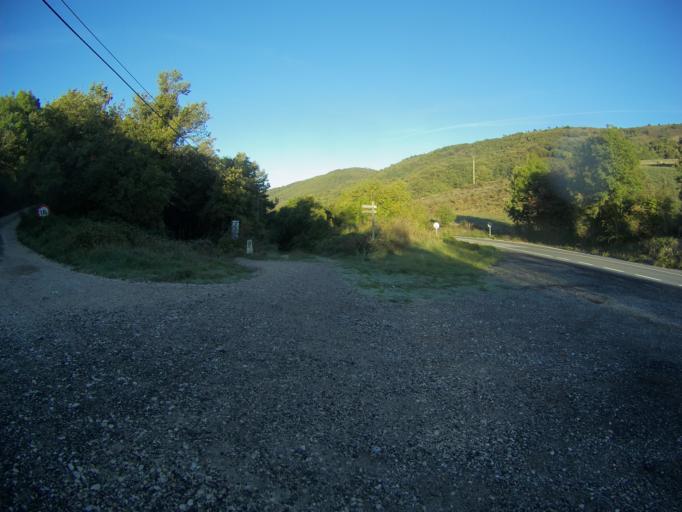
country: ES
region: Navarre
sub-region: Provincia de Navarra
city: Garralda
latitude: 42.9674
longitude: -1.4229
